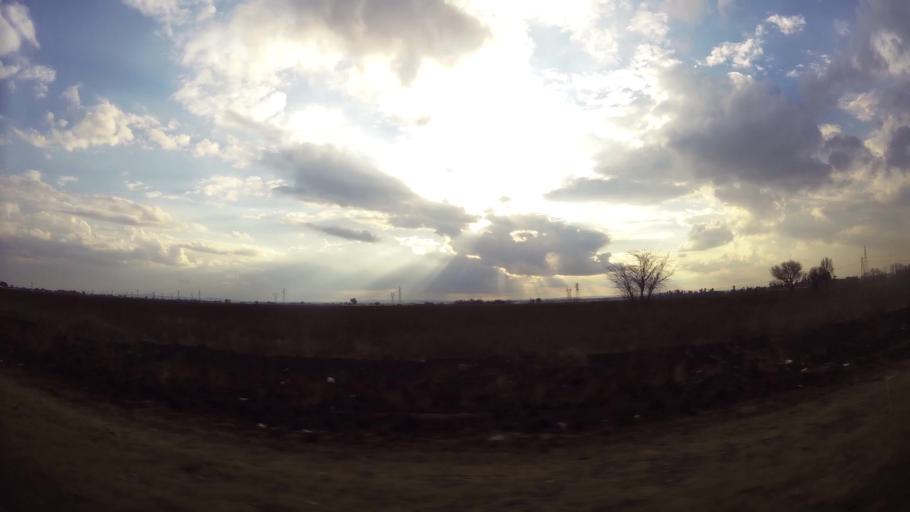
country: ZA
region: Gauteng
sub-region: Sedibeng District Municipality
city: Vanderbijlpark
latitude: -26.6677
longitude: 27.7951
